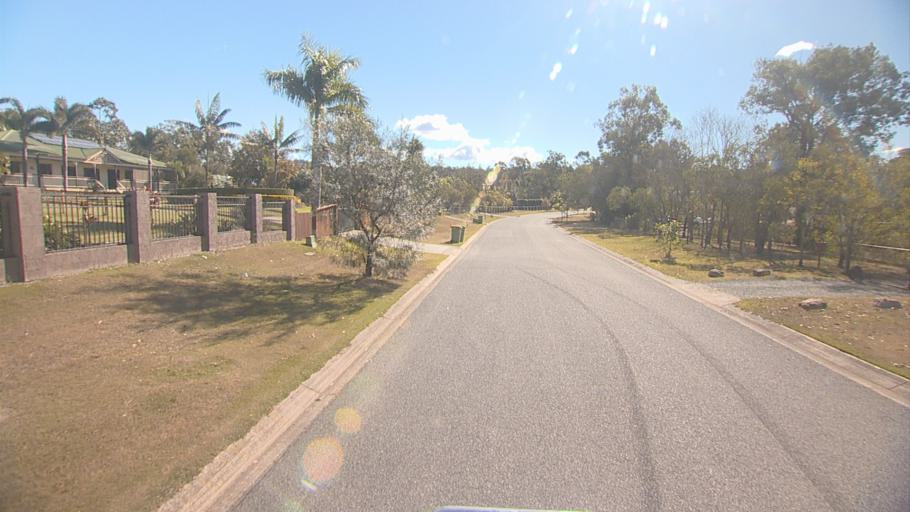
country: AU
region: Queensland
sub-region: Ipswich
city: Springfield Lakes
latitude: -27.7263
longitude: 152.9178
